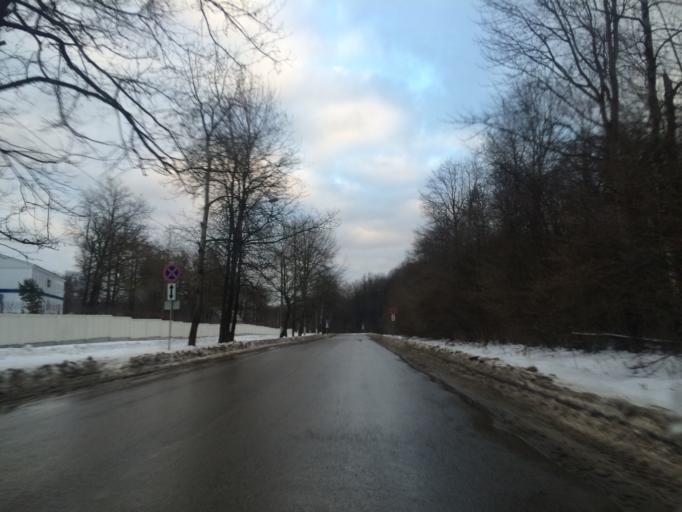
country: RU
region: Tula
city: Tula
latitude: 54.2179
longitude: 37.7090
